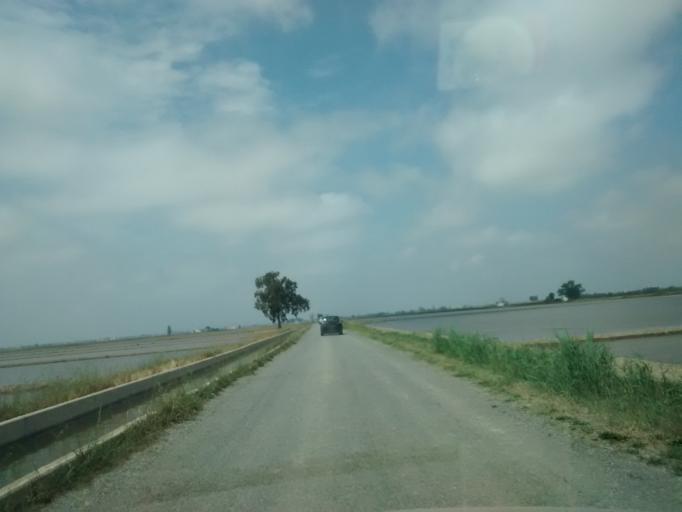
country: ES
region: Catalonia
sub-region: Provincia de Tarragona
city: Deltebre
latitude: 40.6854
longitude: 0.7871
